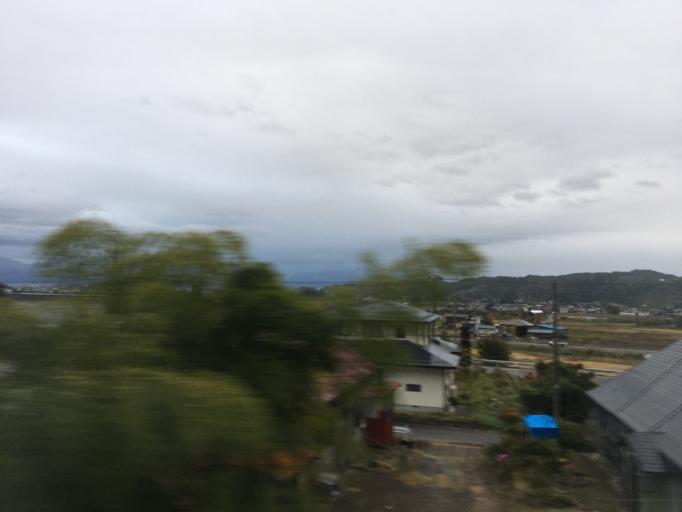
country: JP
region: Yamagata
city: Sagae
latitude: 38.3807
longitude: 140.2318
